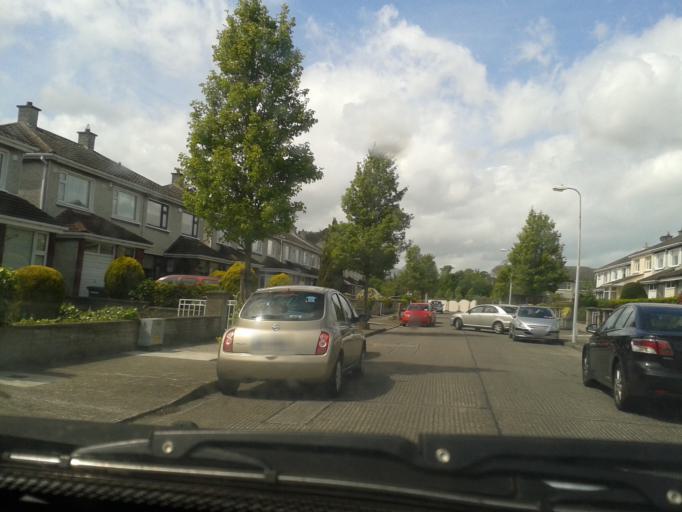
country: IE
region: Leinster
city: Drumcondra
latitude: 53.3779
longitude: -6.2553
